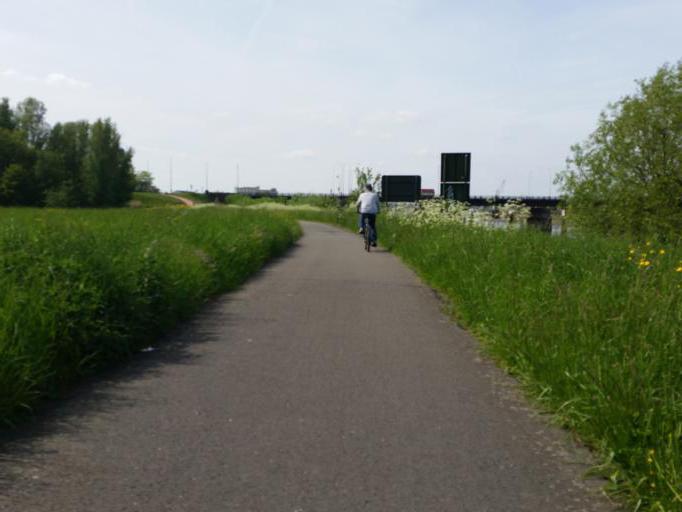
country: BE
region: Flanders
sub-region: Provincie Antwerpen
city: Boom
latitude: 51.0825
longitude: 4.3631
